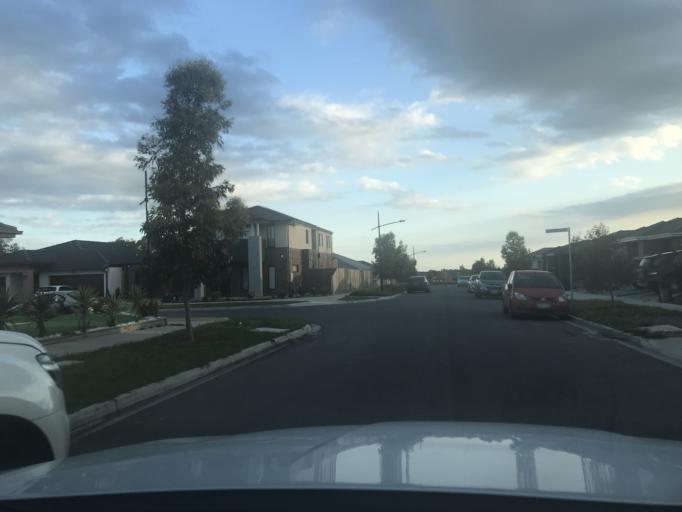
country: AU
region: Victoria
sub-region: Hume
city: Greenvale
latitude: -37.5737
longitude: 144.8887
